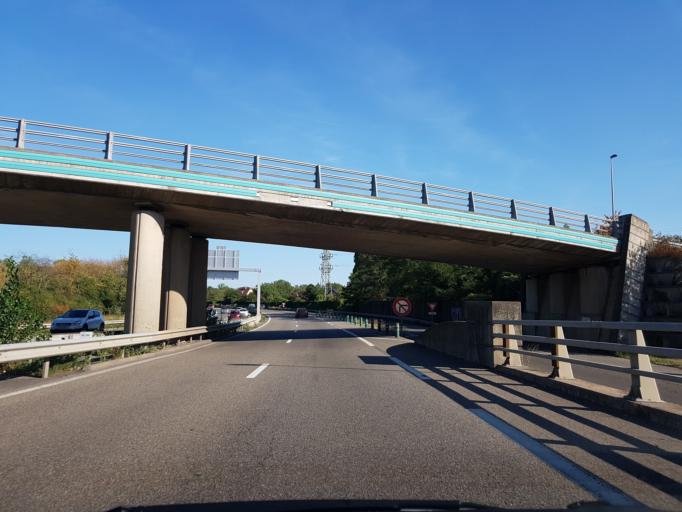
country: FR
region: Alsace
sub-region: Departement du Haut-Rhin
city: Kingersheim
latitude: 47.7879
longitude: 7.3166
